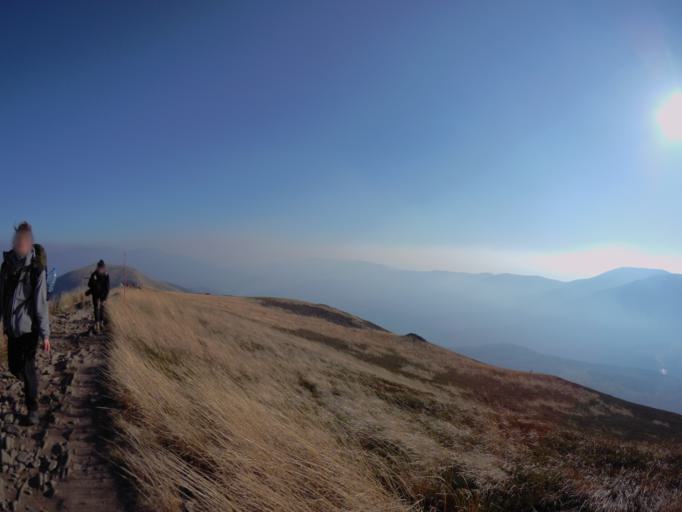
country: PL
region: Subcarpathian Voivodeship
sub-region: Powiat bieszczadzki
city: Lutowiska
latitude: 49.1379
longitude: 22.6039
